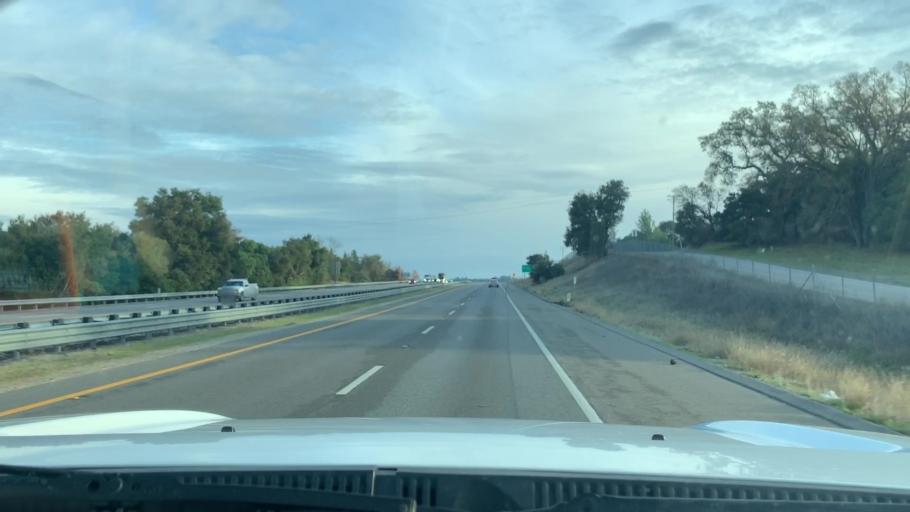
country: US
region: California
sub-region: San Luis Obispo County
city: Atascadero
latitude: 35.4600
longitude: -120.6468
